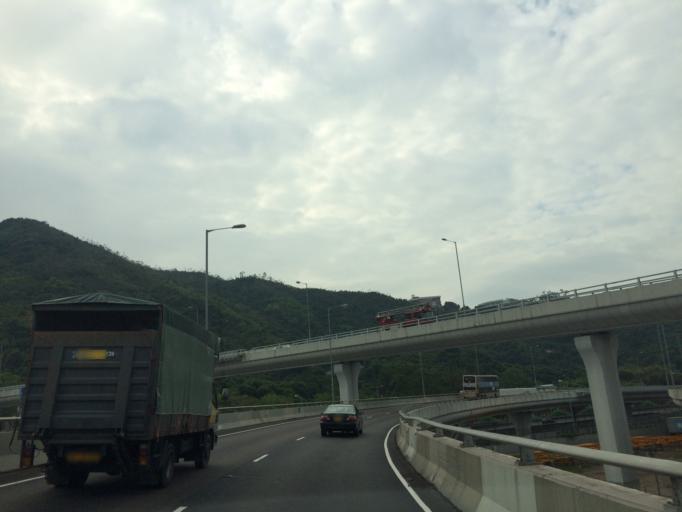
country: HK
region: Sha Tin
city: Sha Tin
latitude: 22.4052
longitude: 114.2184
